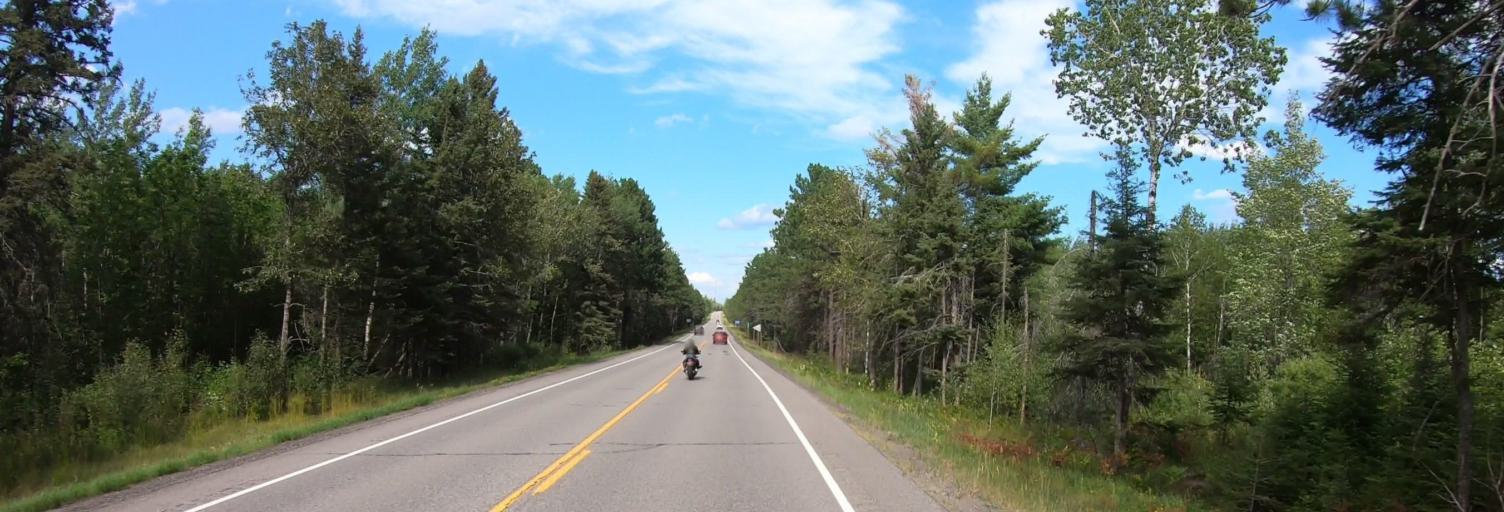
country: US
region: Minnesota
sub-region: Saint Louis County
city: Babbitt
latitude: 47.8242
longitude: -92.1861
